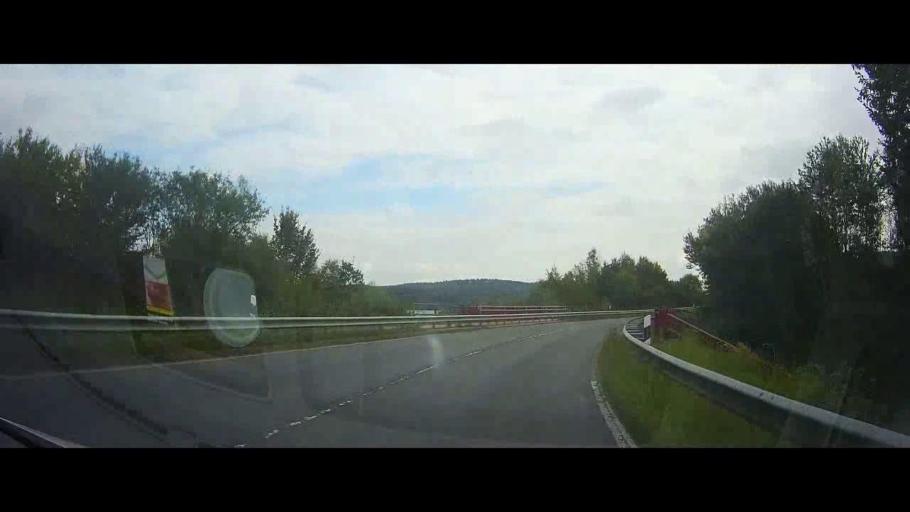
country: DE
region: Lower Saxony
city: Adelebsen
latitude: 51.5735
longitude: 9.7489
